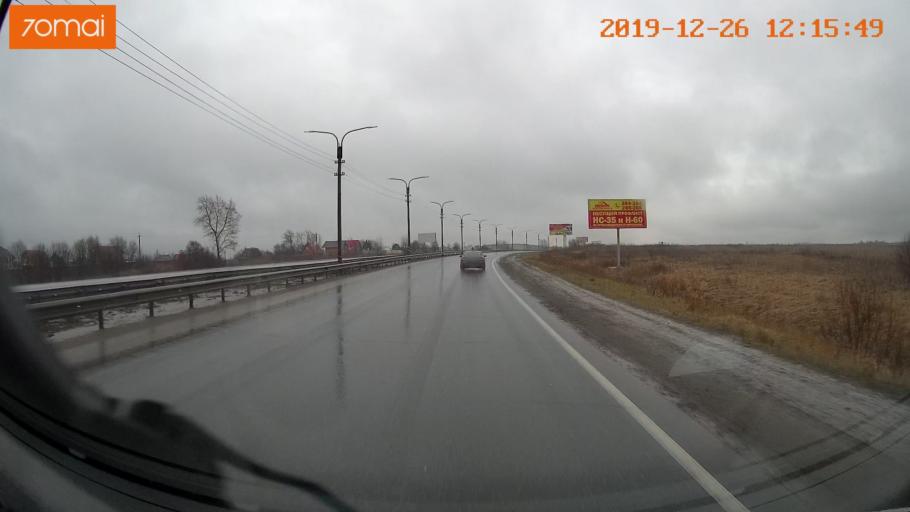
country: RU
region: Vologda
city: Tonshalovo
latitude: 59.2033
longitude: 37.9416
